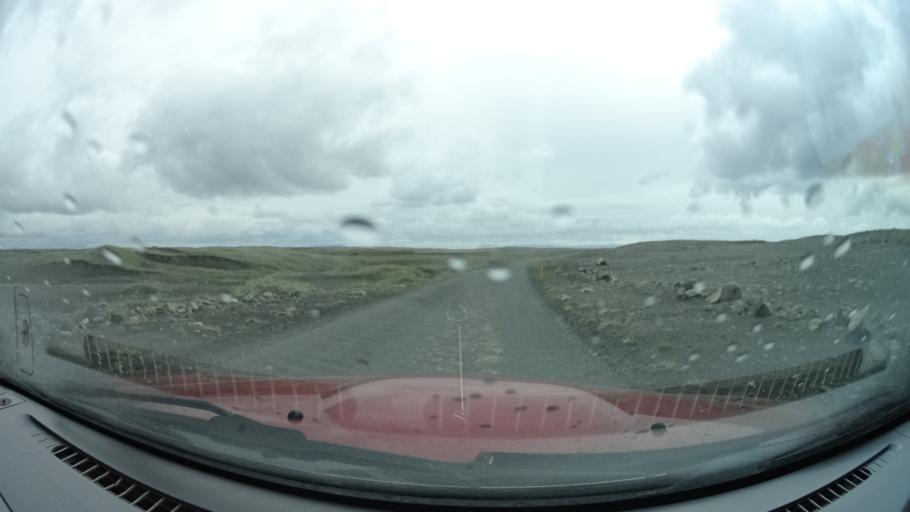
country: IS
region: Northeast
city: Laugar
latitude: 65.7553
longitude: -16.3312
